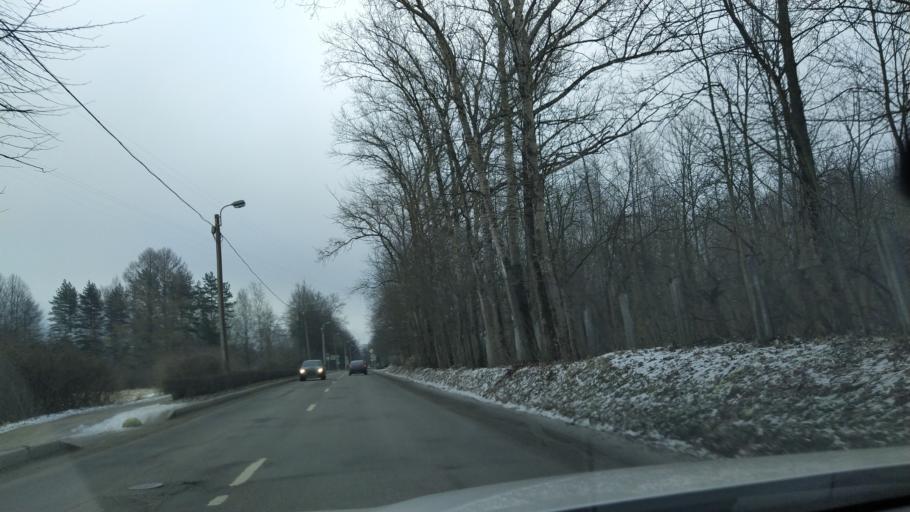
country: RU
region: St.-Petersburg
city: Pushkin
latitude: 59.7272
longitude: 30.3918
